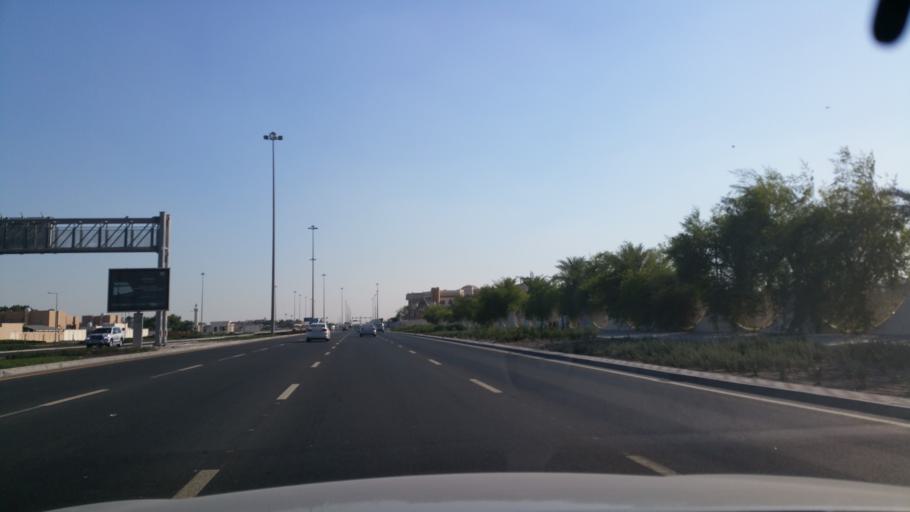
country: QA
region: Baladiyat ar Rayyan
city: Ar Rayyan
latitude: 25.2751
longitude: 51.4311
